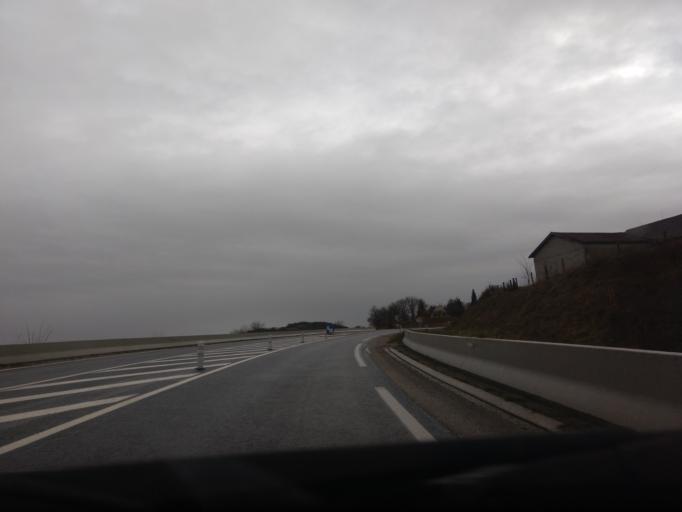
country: FR
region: Midi-Pyrenees
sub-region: Departement de l'Aveyron
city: Firmi
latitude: 44.5145
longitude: 2.3566
